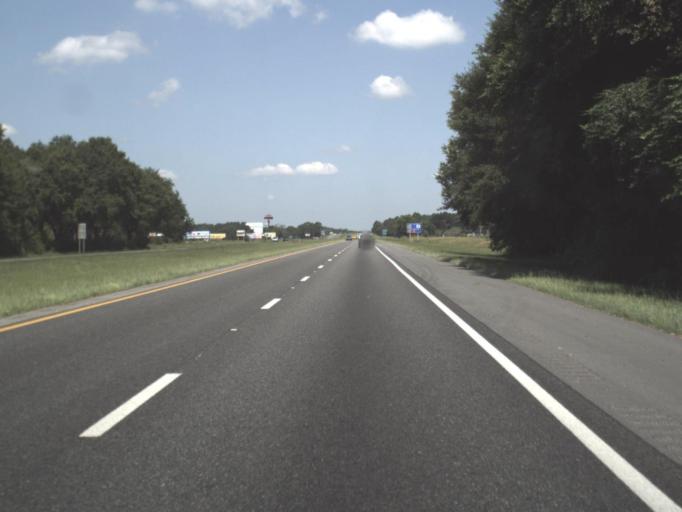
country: US
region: Florida
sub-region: Madison County
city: Madison
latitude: 30.3771
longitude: -83.2850
